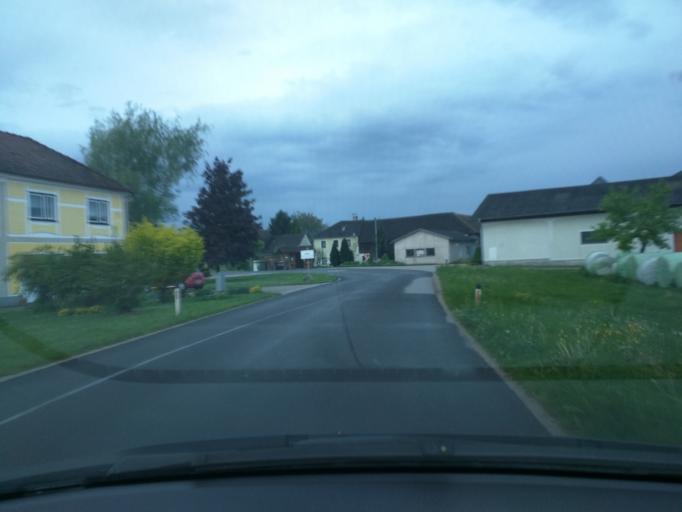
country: AT
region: Lower Austria
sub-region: Politischer Bezirk Amstetten
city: Sankt Georgen am Ybbsfelde
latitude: 48.1183
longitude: 14.9497
